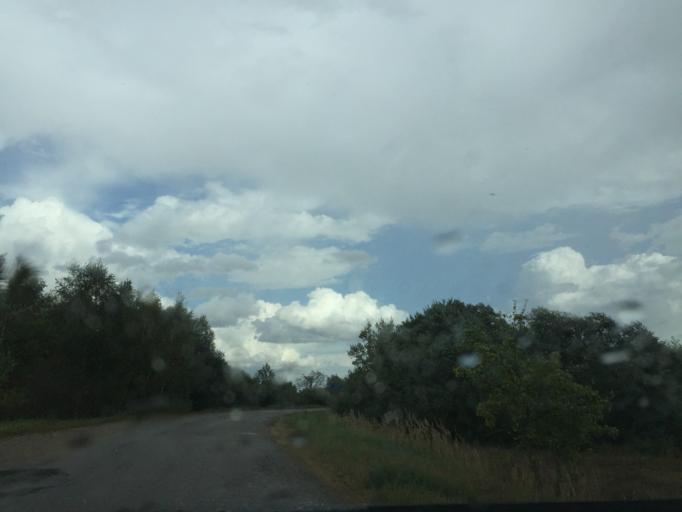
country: LV
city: Tervete
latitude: 56.3672
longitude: 23.4971
